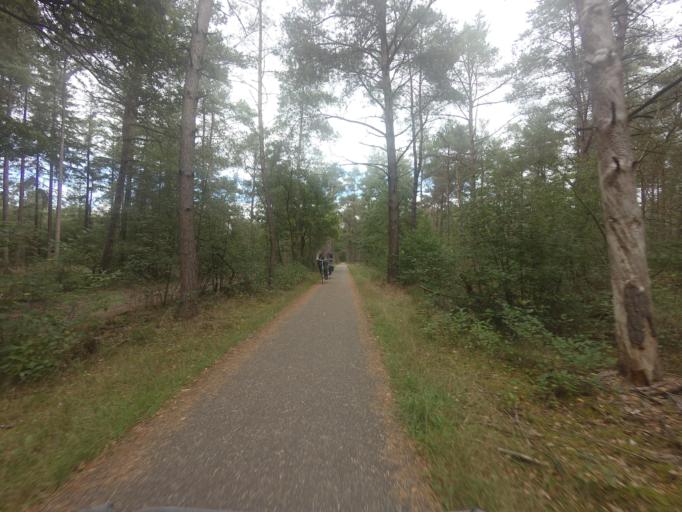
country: NL
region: Friesland
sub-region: Gemeente Weststellingwerf
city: Noordwolde
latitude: 52.9019
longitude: 6.2415
